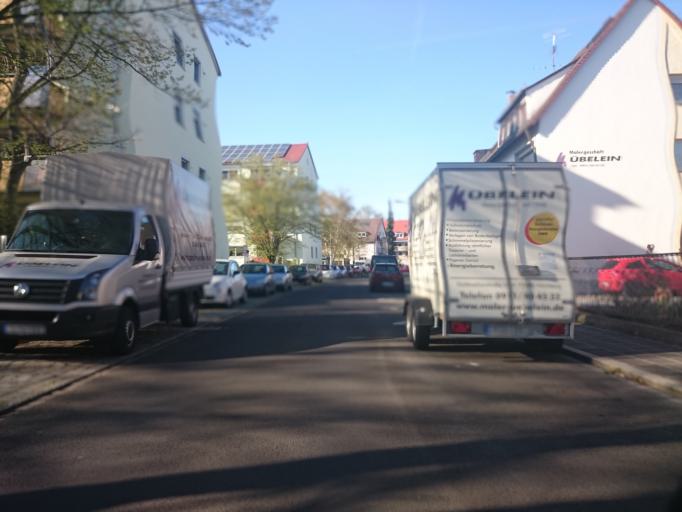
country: DE
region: Bavaria
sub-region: Regierungsbezirk Mittelfranken
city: Nuernberg
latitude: 49.4493
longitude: 11.1243
